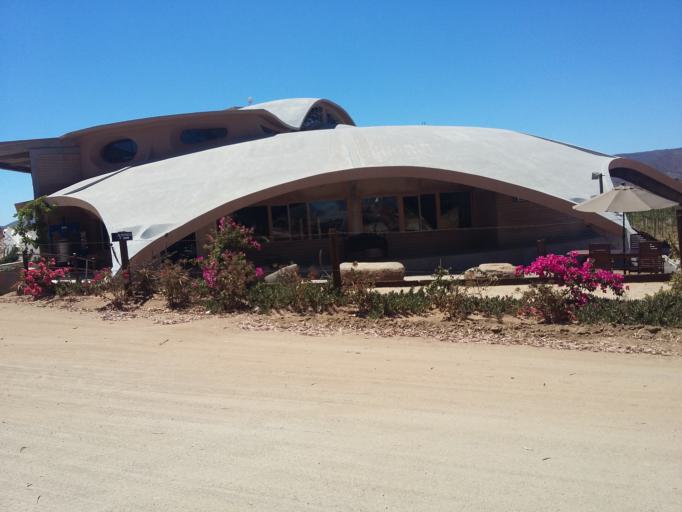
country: MX
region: Baja California
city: El Sauzal
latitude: 32.0022
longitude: -116.6703
